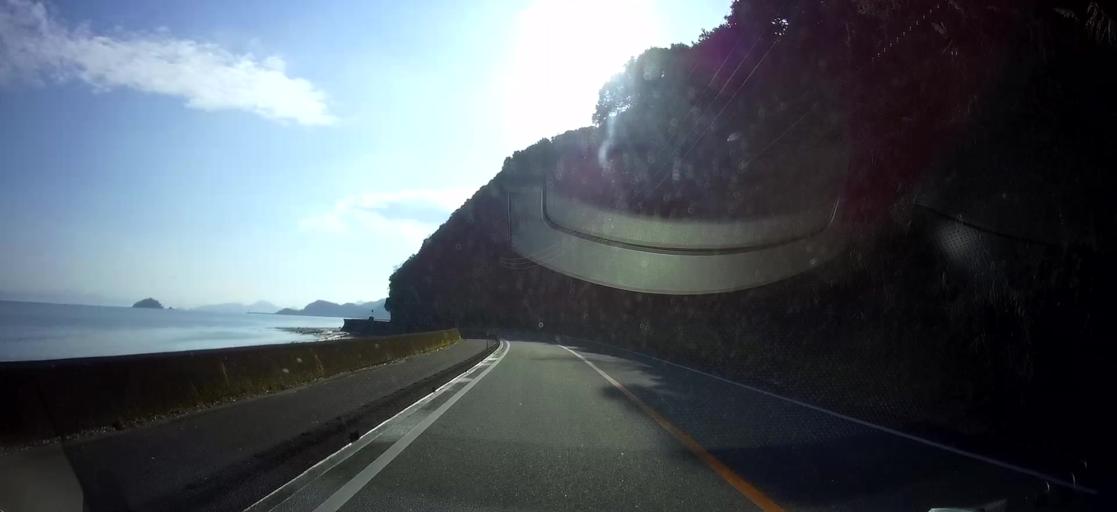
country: JP
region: Kumamoto
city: Yatsushiro
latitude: 32.4945
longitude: 130.4437
